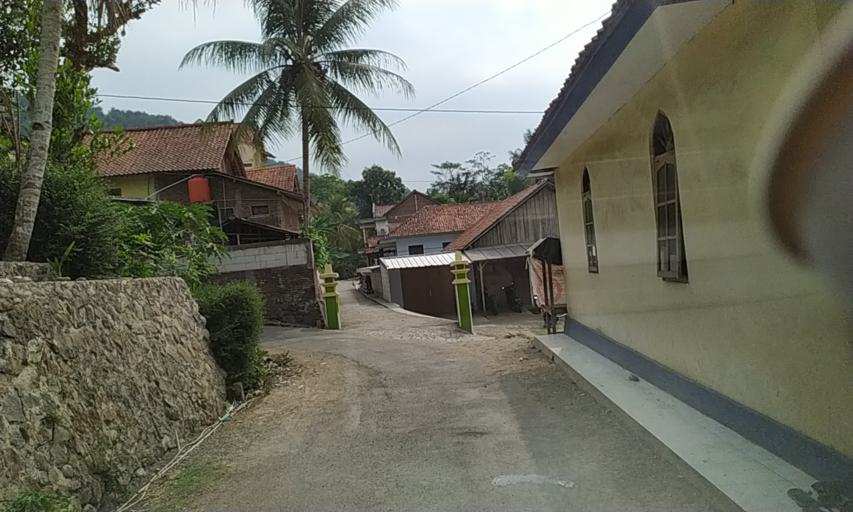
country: ID
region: Central Java
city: Telagasari
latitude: -7.3050
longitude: 108.8320
